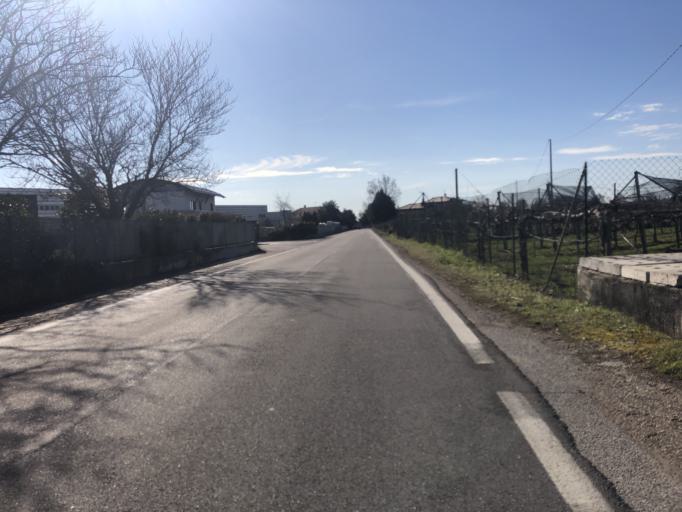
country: IT
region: Veneto
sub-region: Provincia di Verona
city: Ospedaletto
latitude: 45.5075
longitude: 10.8339
